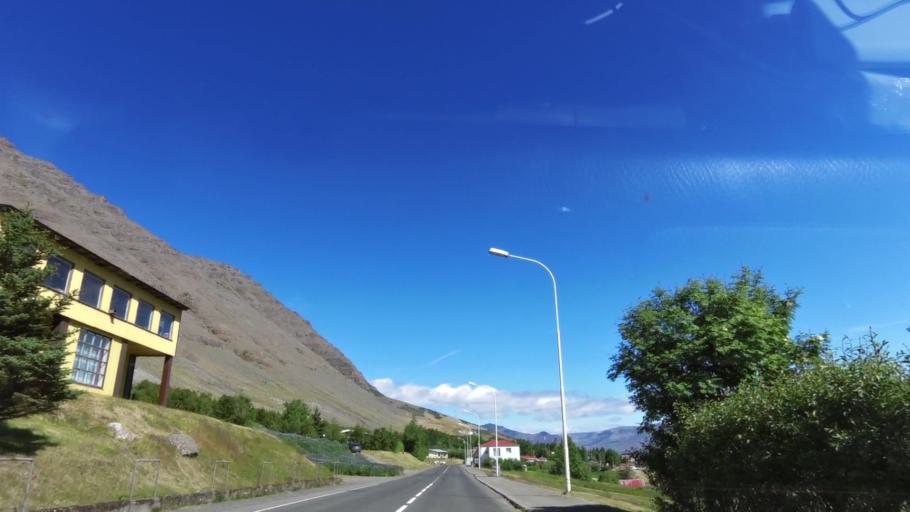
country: IS
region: Westfjords
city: Isafjoerdur
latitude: 65.6809
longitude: -23.6098
